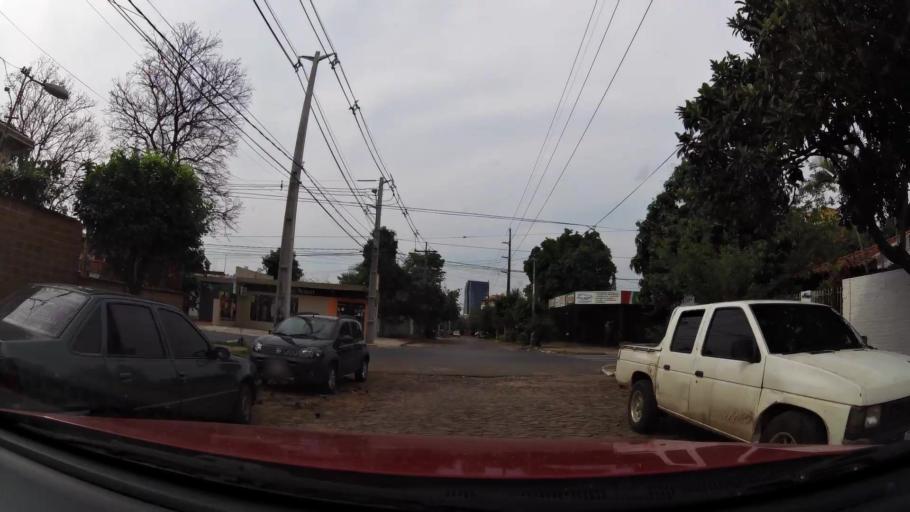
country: PY
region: Central
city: Fernando de la Mora
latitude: -25.2918
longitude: -57.5671
